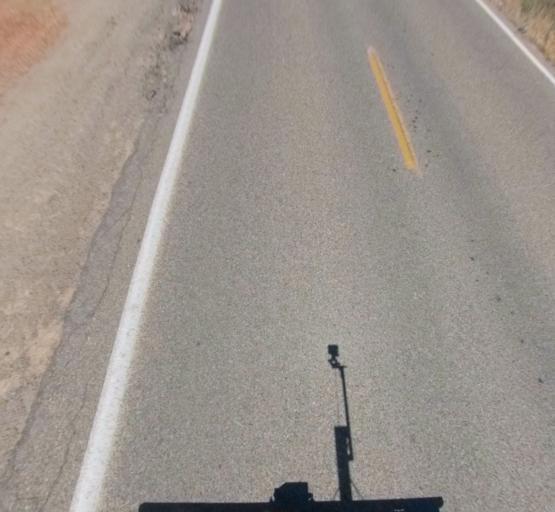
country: US
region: California
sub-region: Madera County
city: Fairmead
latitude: 37.0183
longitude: -120.2374
